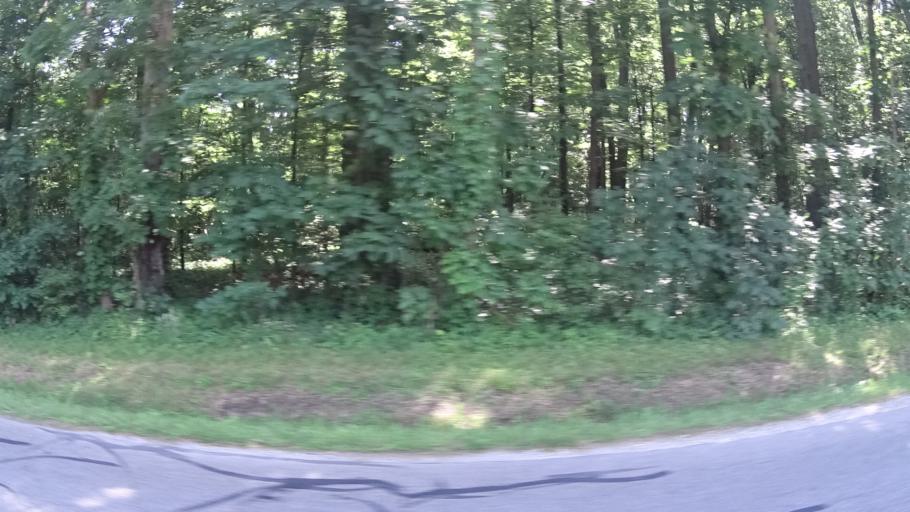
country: US
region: Ohio
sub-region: Erie County
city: Huron
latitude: 41.3597
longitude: -82.4578
